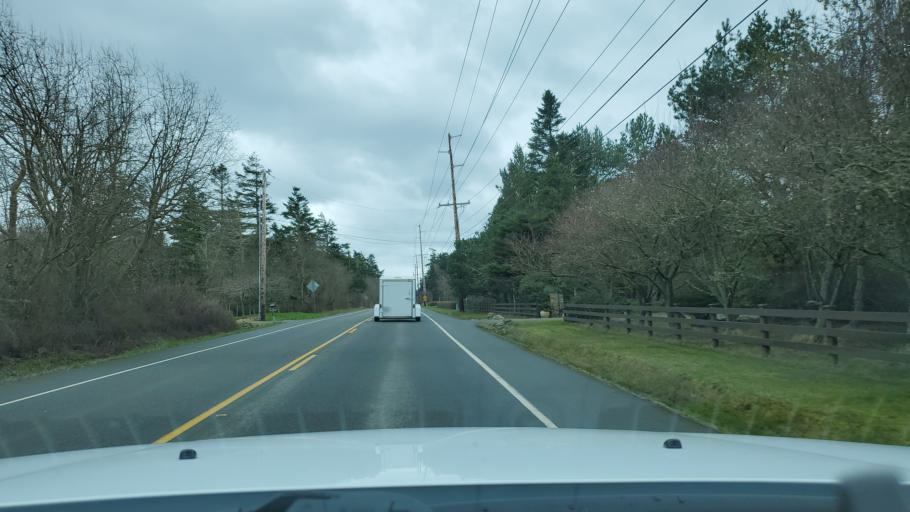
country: US
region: Washington
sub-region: Island County
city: Coupeville
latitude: 48.2563
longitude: -122.7517
